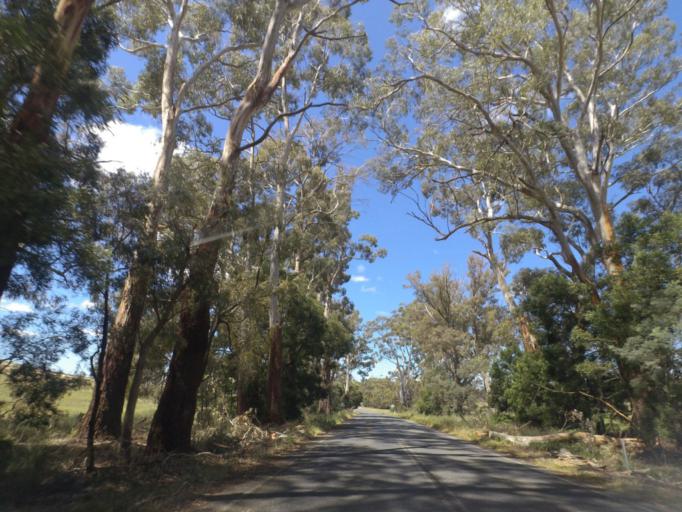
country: AU
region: Victoria
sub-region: Mount Alexander
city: Castlemaine
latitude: -37.3154
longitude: 144.2225
